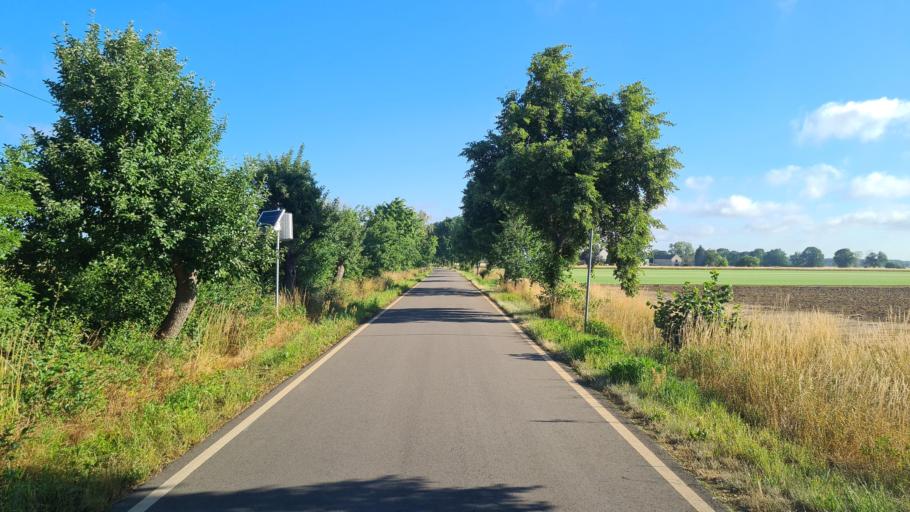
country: DE
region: Saxony
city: Beilrode
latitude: 51.6089
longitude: 13.1230
